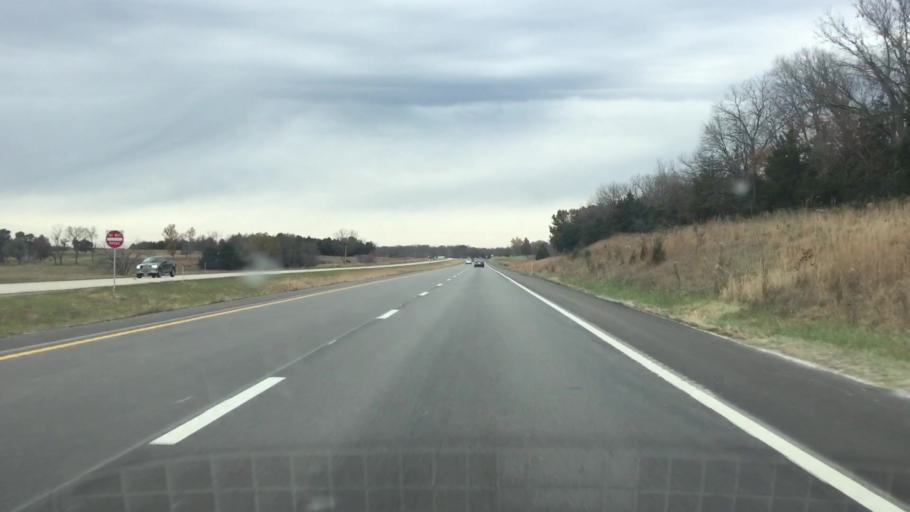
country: US
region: Missouri
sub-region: Saint Clair County
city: Osceola
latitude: 38.0014
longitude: -93.6551
